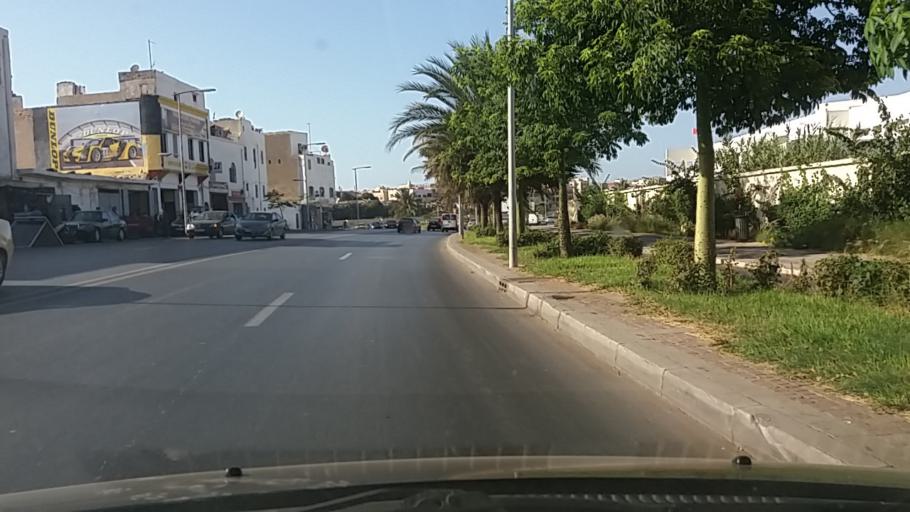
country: MA
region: Rabat-Sale-Zemmour-Zaer
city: Sale
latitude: 34.0443
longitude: -6.8178
